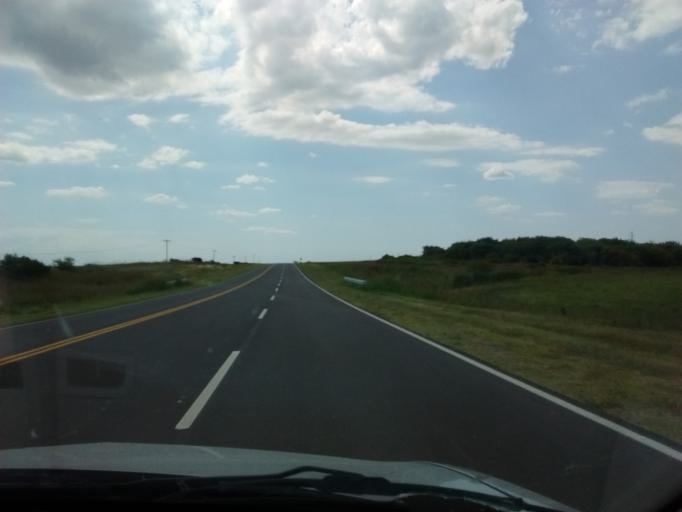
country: AR
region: Entre Rios
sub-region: Departamento de Victoria
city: Victoria
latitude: -32.6702
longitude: -60.0357
